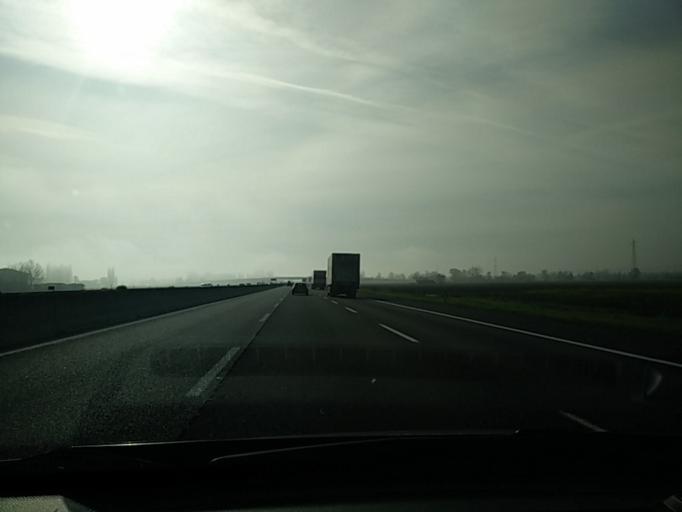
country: IT
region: Emilia-Romagna
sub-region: Provincia di Bologna
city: Osteria Grande
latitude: 44.4471
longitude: 11.5489
